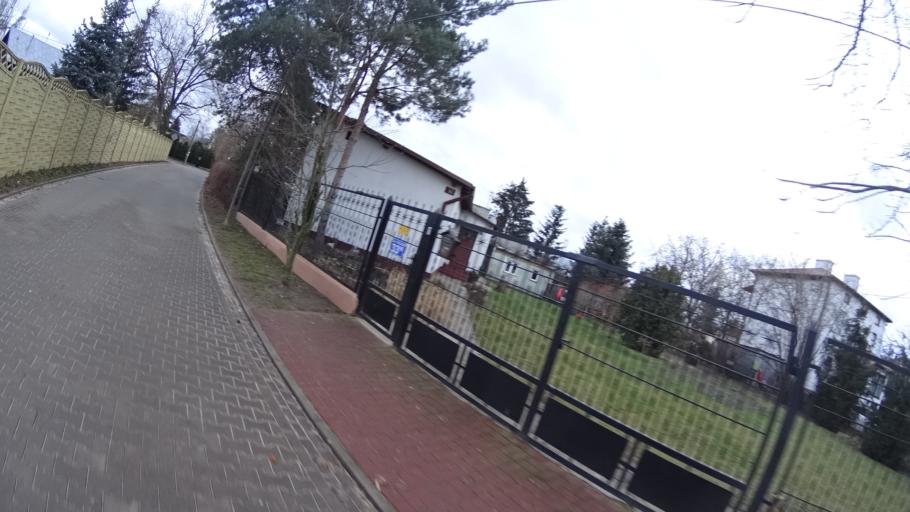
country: PL
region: Masovian Voivodeship
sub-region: Powiat pruszkowski
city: Granica
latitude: 52.1453
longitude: 20.7950
